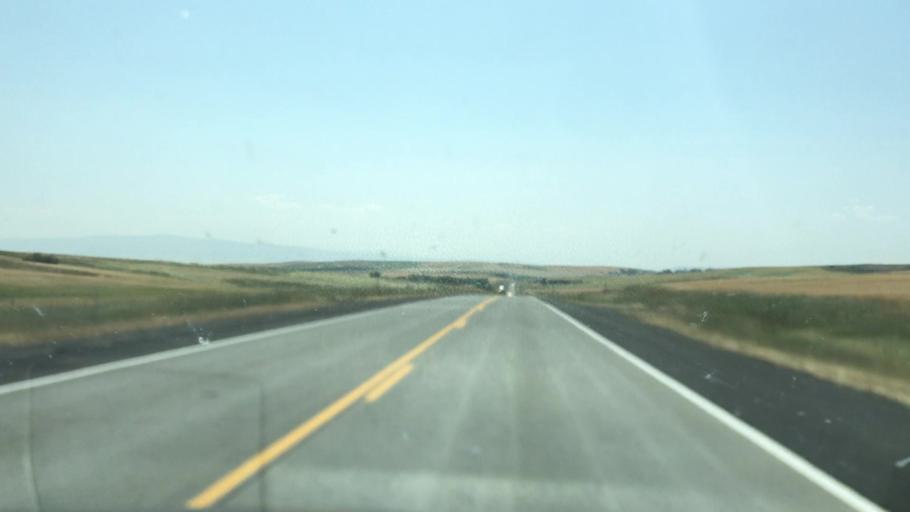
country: US
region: Idaho
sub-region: Lewis County
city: Nezperce
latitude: 46.0915
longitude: -116.3479
